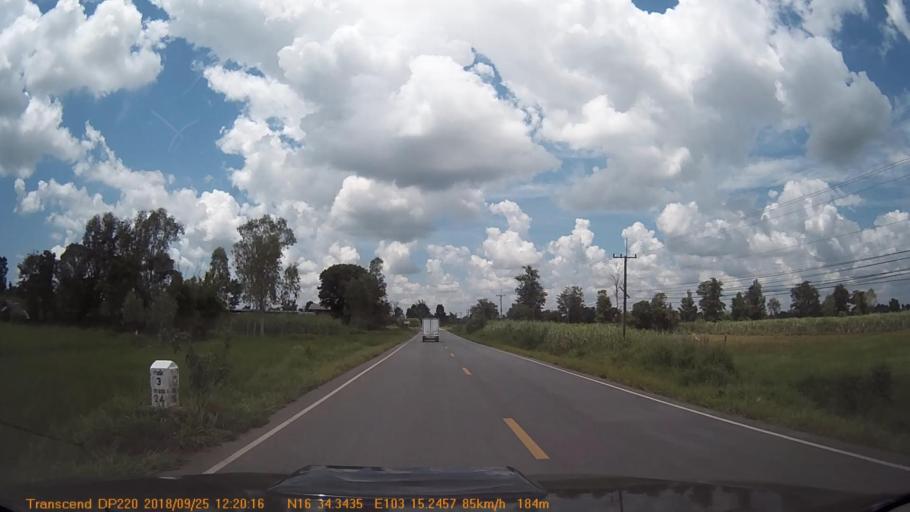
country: TH
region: Kalasin
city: Huai Mek
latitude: 16.5723
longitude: 103.2542
